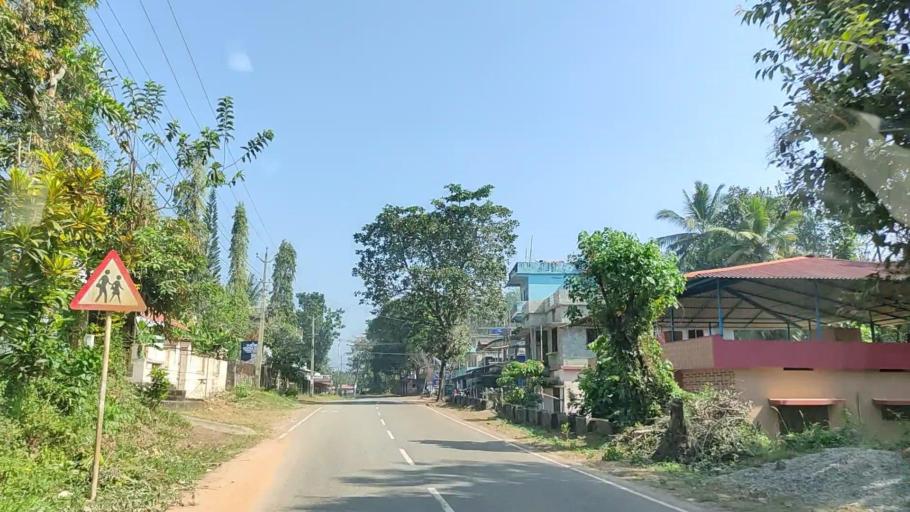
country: IN
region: Kerala
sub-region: Kollam
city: Punalur
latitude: 8.9211
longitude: 77.0585
